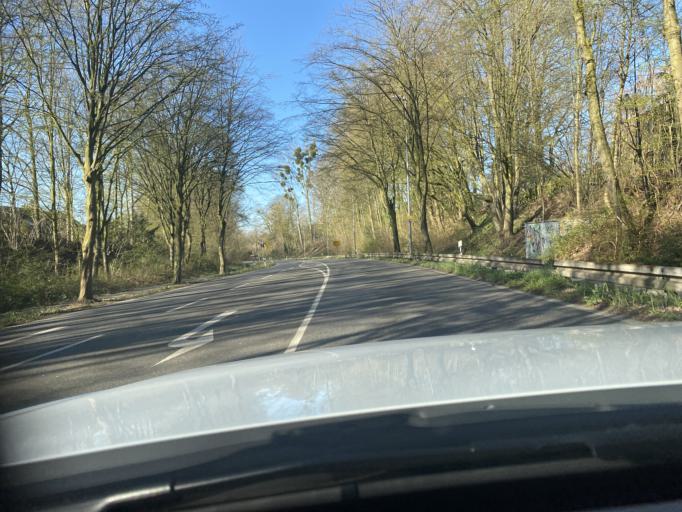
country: DE
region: North Rhine-Westphalia
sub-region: Regierungsbezirk Dusseldorf
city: Ratingen
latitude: 51.2565
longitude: 6.8687
